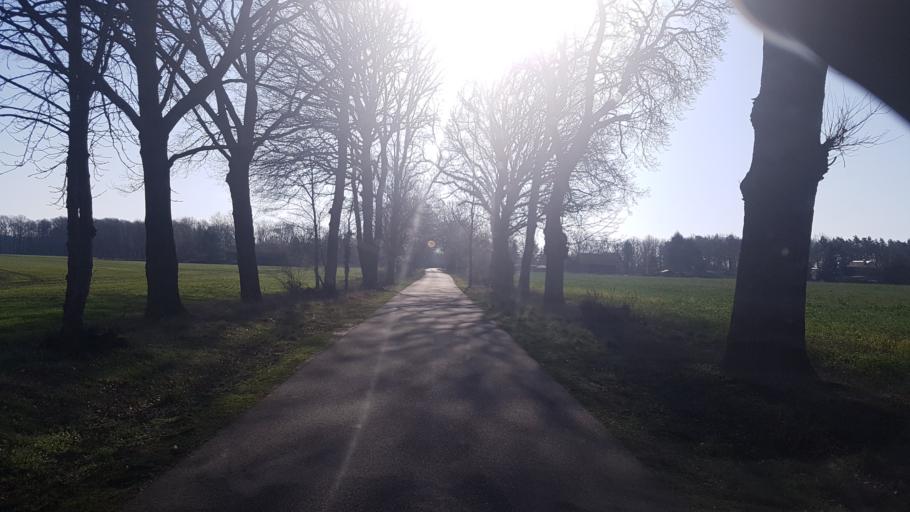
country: DE
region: Brandenburg
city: Luckau
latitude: 51.8379
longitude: 13.7901
